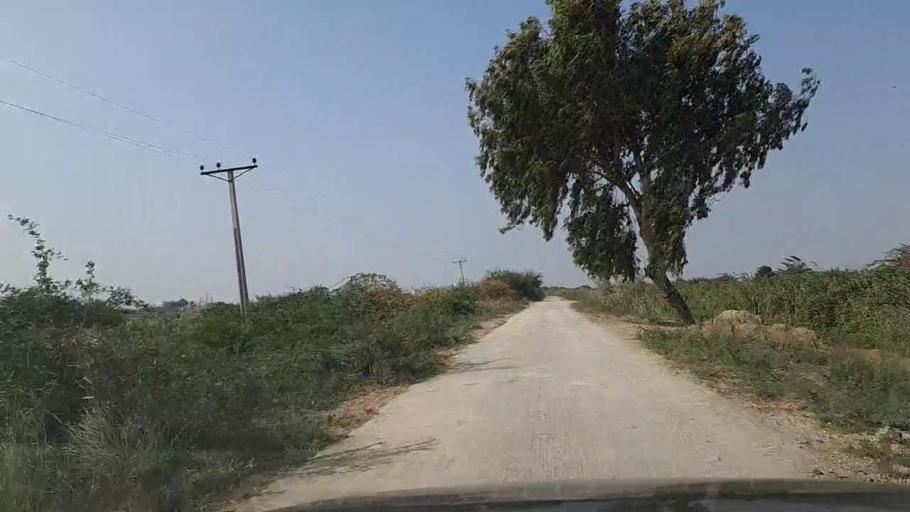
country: PK
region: Sindh
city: Gharo
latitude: 24.7359
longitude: 67.7452
